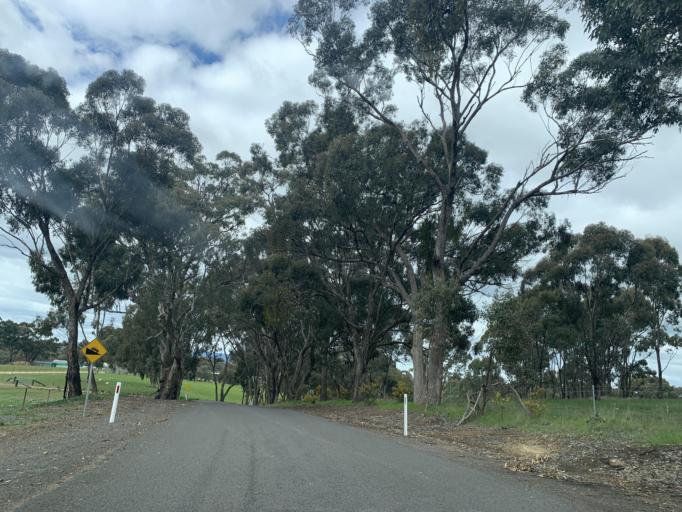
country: AU
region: Victoria
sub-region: Whittlesea
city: Whittlesea
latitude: -37.1206
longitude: 144.9341
